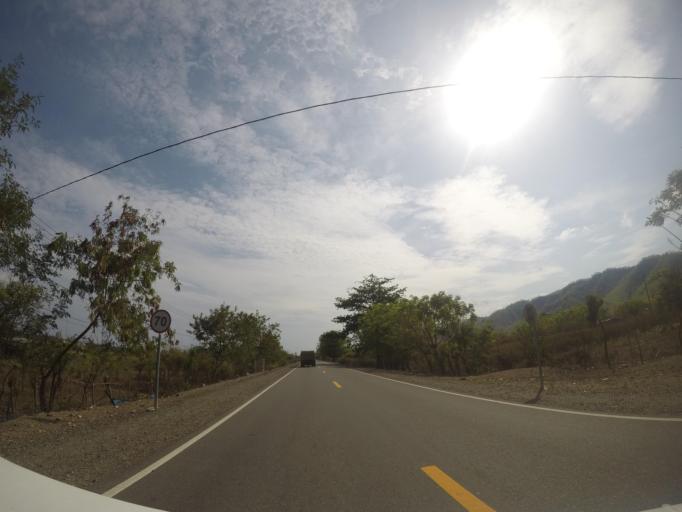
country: ID
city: Metinaro
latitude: -8.5249
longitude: 125.7640
